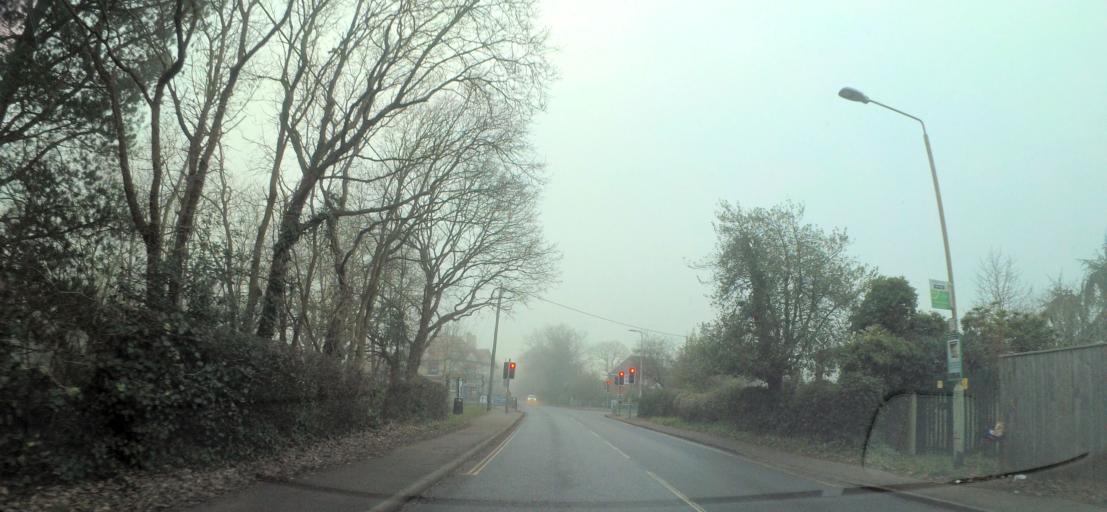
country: GB
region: England
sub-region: West Berkshire
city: Stratfield Mortimer
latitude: 51.3940
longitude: -1.0661
